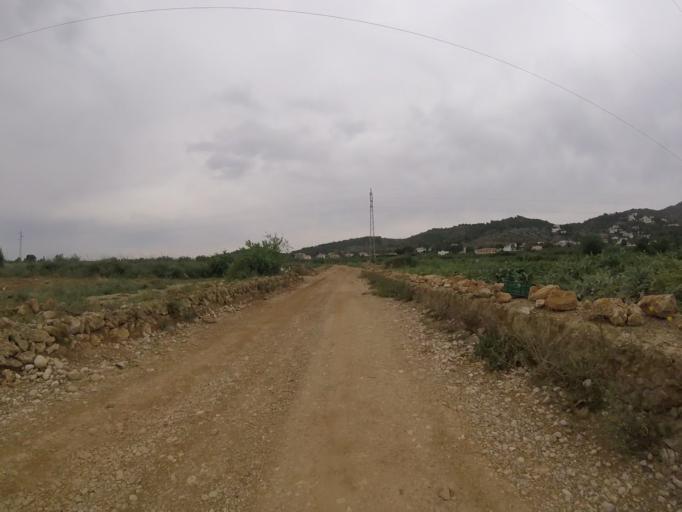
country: ES
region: Valencia
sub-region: Provincia de Castello
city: Alcoceber
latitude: 40.2443
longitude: 0.2597
